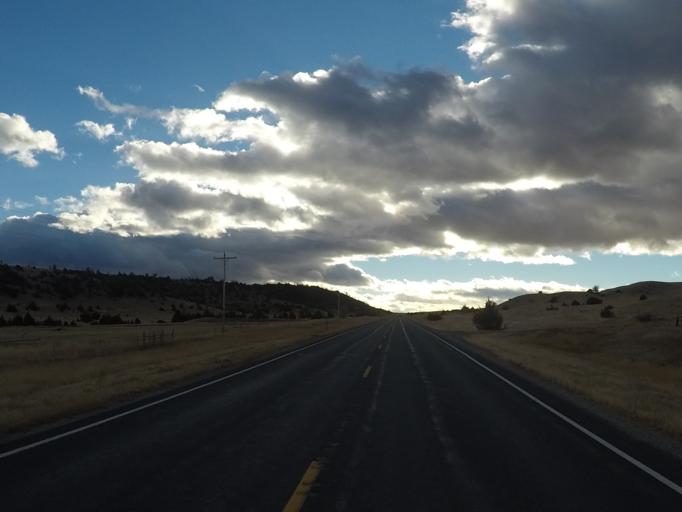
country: US
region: Montana
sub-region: Jefferson County
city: Whitehall
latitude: 45.9079
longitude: -111.9443
